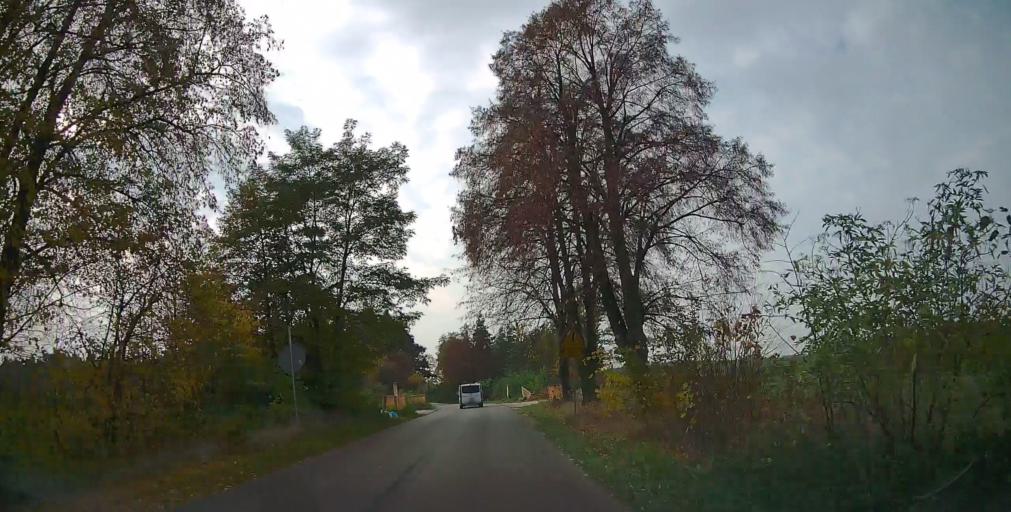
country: PL
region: Masovian Voivodeship
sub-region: Powiat grojecki
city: Mogielnica
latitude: 51.6727
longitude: 20.7122
